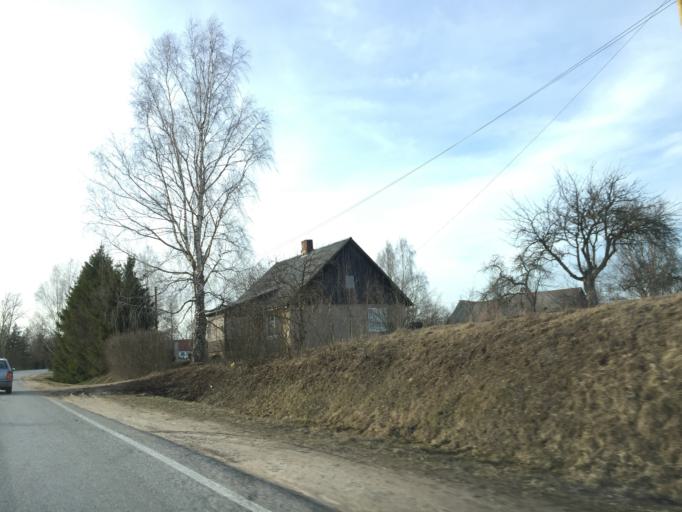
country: LV
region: Krimulda
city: Ragana
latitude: 57.1769
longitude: 24.7180
